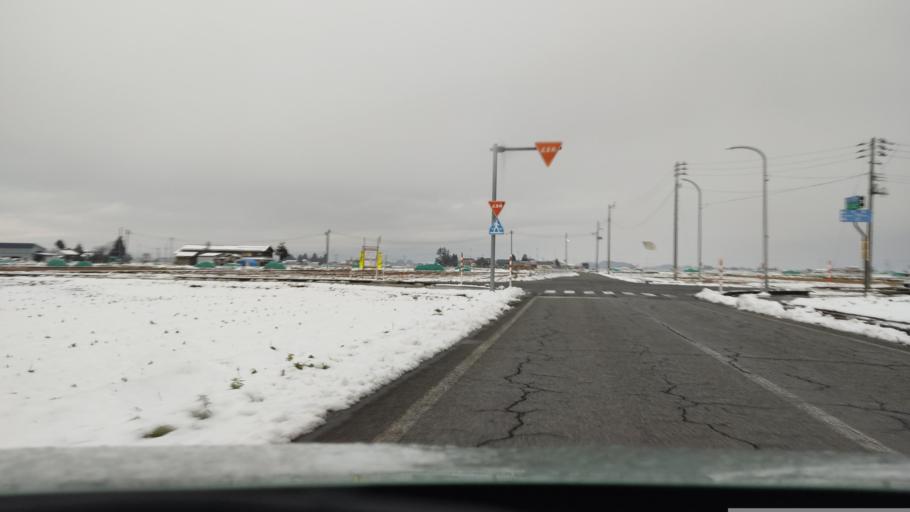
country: JP
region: Akita
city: Omagari
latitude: 39.4288
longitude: 140.5357
